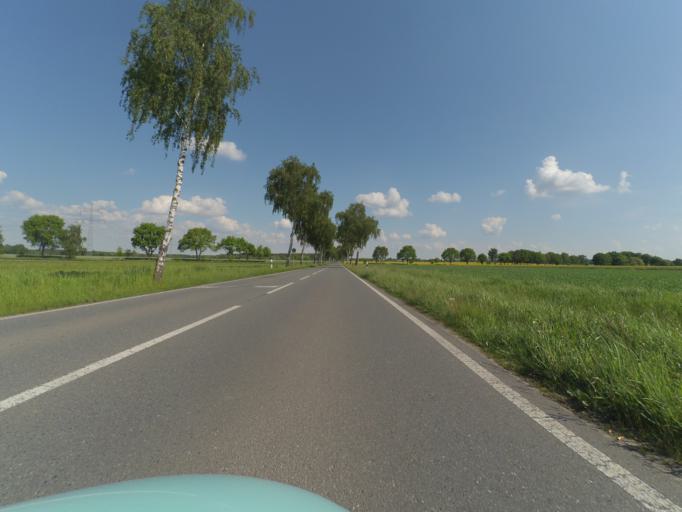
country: DE
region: Lower Saxony
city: Isernhagen Farster Bauerschaft
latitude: 52.4805
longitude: 9.8980
